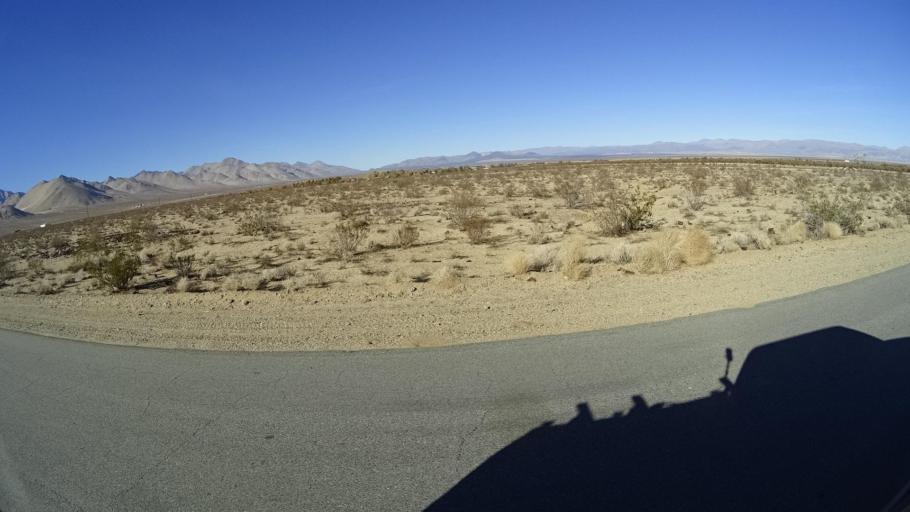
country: US
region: California
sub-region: Kern County
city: Inyokern
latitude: 35.6793
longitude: -117.8417
